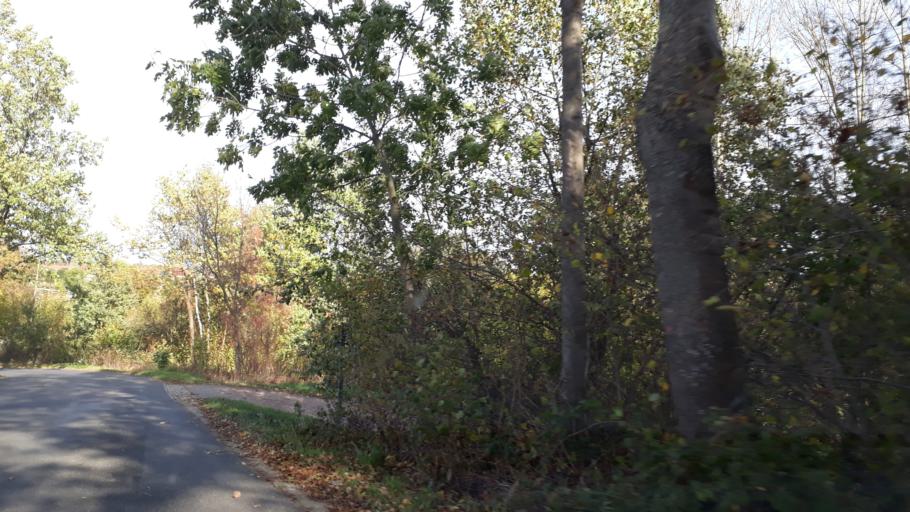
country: DE
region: Saxony
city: Ebersbach
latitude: 51.1097
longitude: 13.1376
